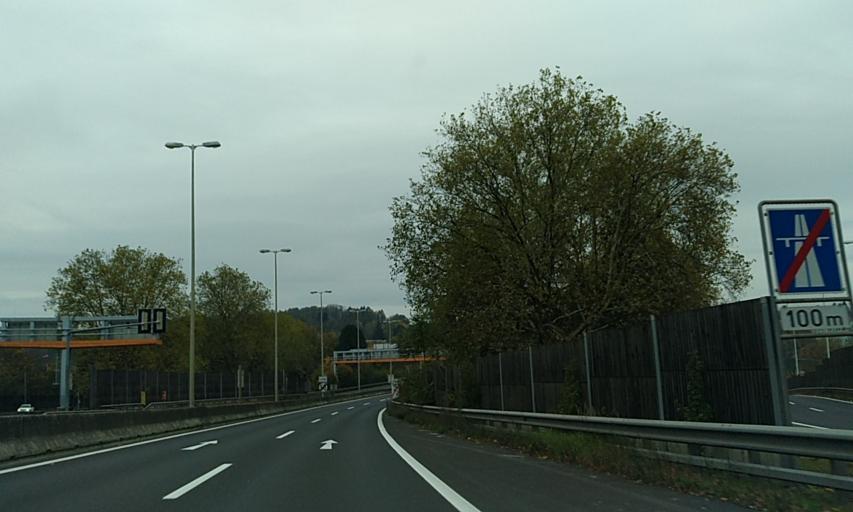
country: AT
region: Upper Austria
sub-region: Linz Stadt
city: Linz
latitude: 48.2806
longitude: 14.2888
